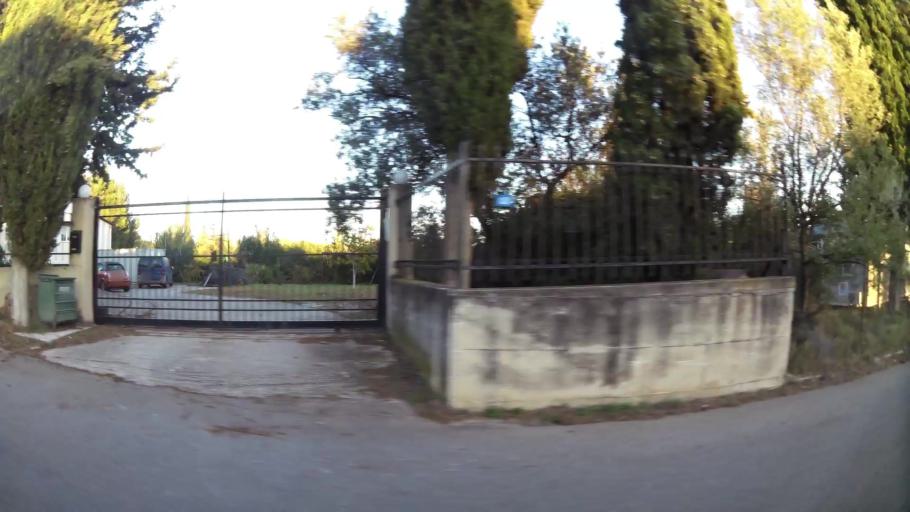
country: GR
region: Attica
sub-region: Nomarchia Anatolikis Attikis
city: Kryoneri
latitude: 38.1439
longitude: 23.8421
